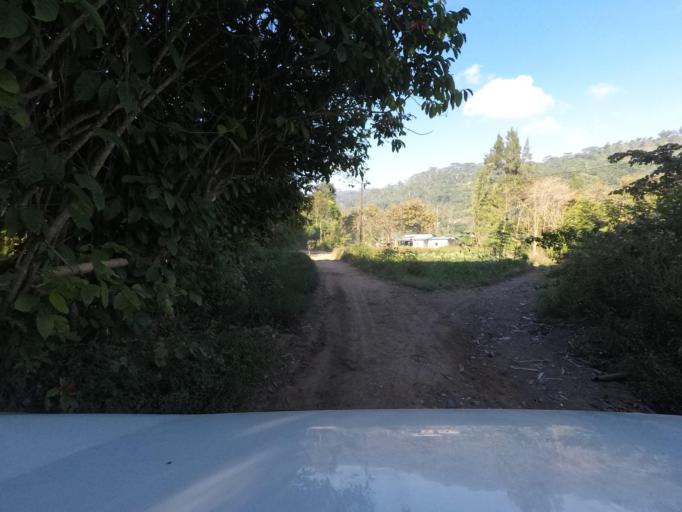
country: TL
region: Ermera
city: Gleno
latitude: -8.7328
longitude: 125.4318
